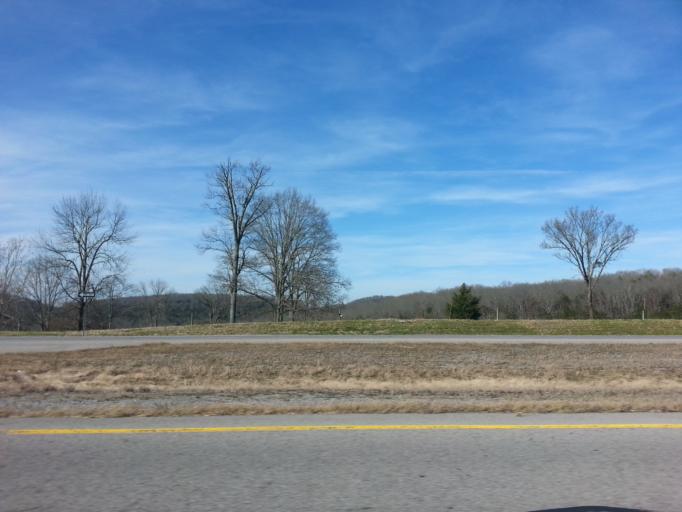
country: US
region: Tennessee
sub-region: Cannon County
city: Woodbury
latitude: 35.8089
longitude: -86.1936
